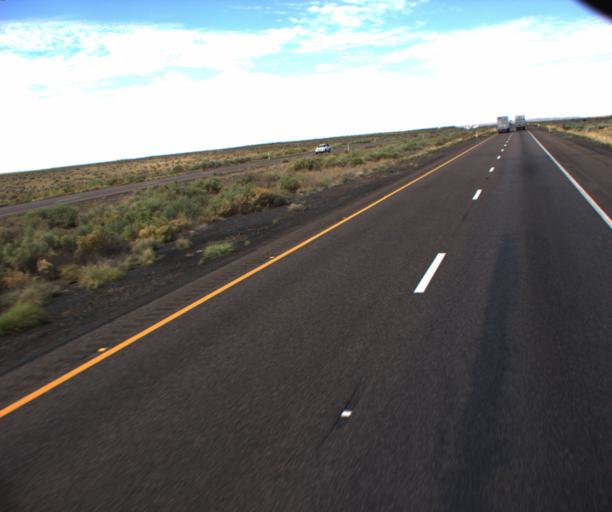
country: US
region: Arizona
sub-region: Apache County
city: Houck
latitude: 35.0965
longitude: -109.6626
